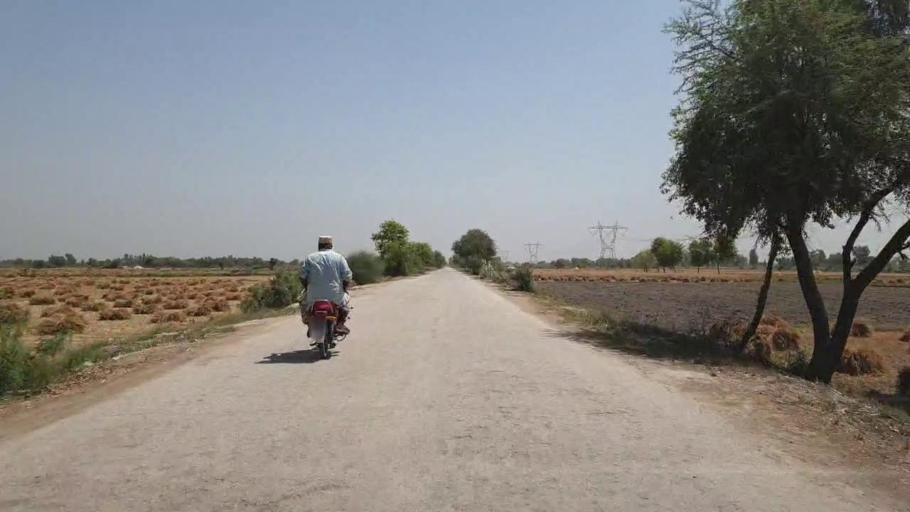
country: PK
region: Sindh
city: Adilpur
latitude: 27.8355
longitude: 69.2602
